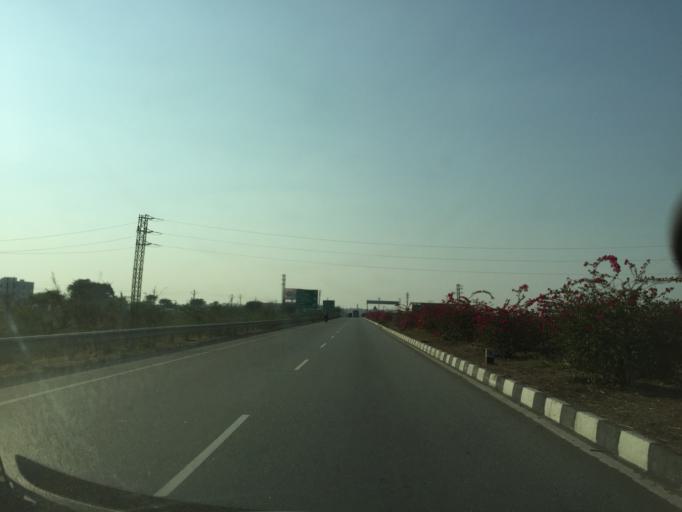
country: IN
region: Telangana
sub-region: Nalgonda
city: Bhongir
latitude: 17.5002
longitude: 78.8865
